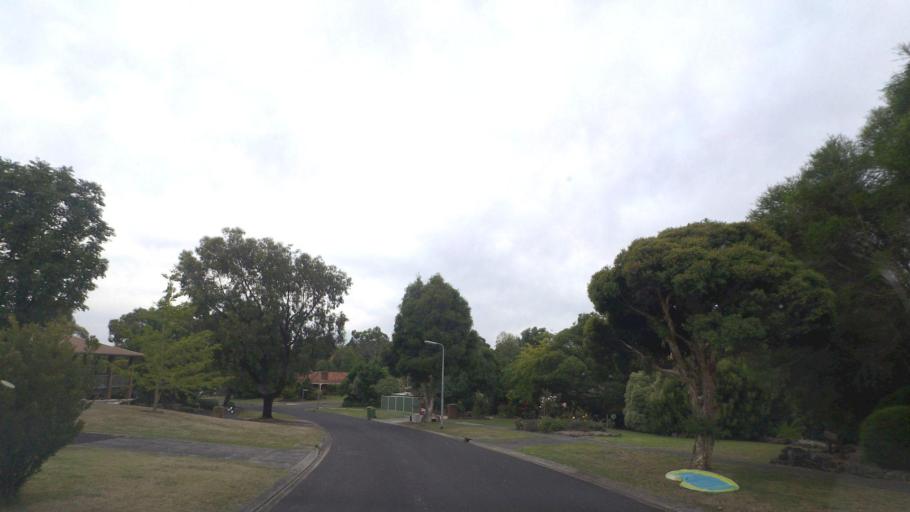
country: AU
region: Victoria
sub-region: Yarra Ranges
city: Kilsyth
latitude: -37.7973
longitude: 145.3357
